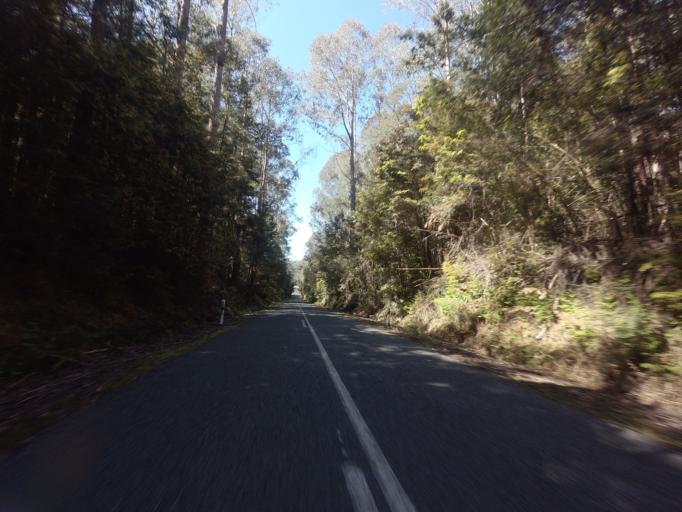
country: AU
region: Tasmania
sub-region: Derwent Valley
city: New Norfolk
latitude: -42.7449
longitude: 146.4151
